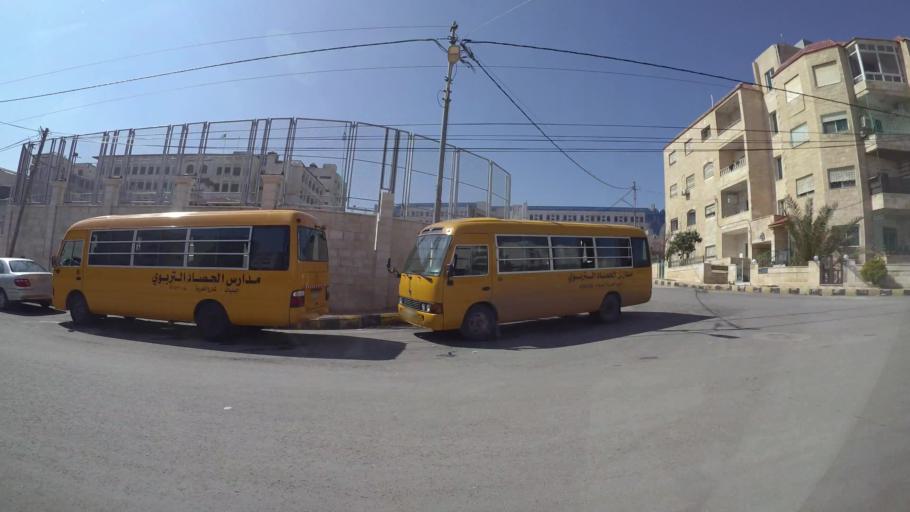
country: JO
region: Amman
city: Al Bunayyat ash Shamaliyah
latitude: 31.8914
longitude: 35.8960
